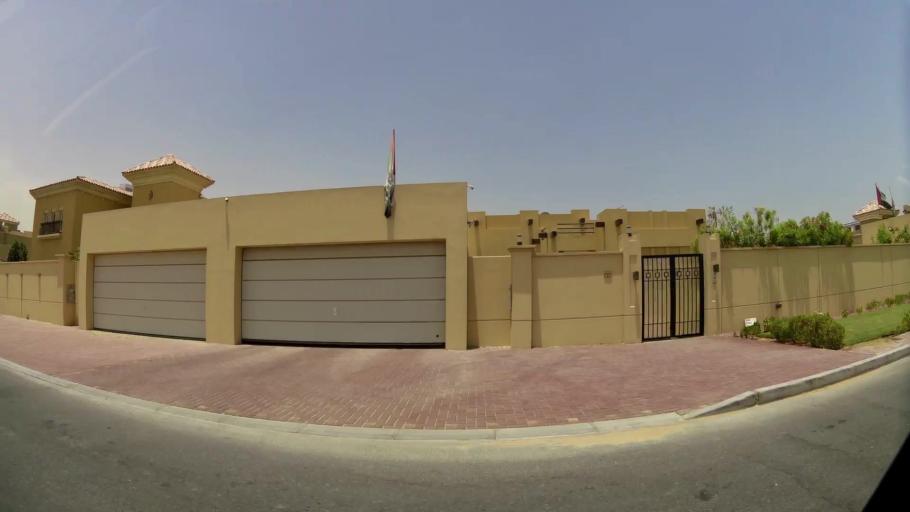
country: AE
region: Dubai
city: Dubai
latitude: 25.0821
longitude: 55.2466
